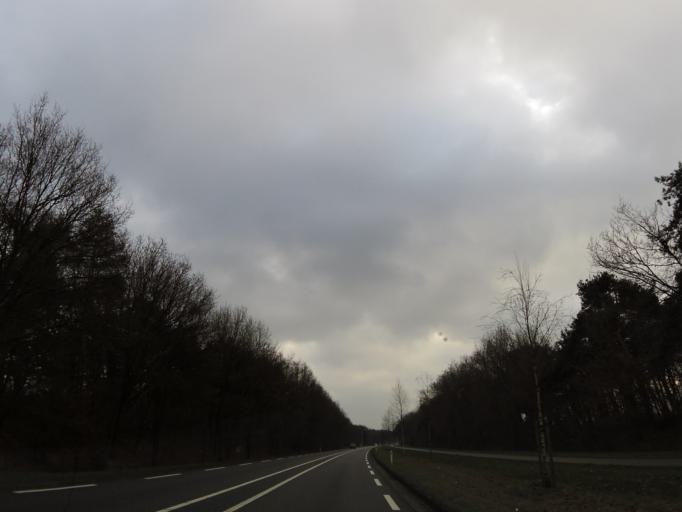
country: NL
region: Limburg
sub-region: Gemeente Venlo
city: Arcen
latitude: 51.4864
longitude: 6.1884
